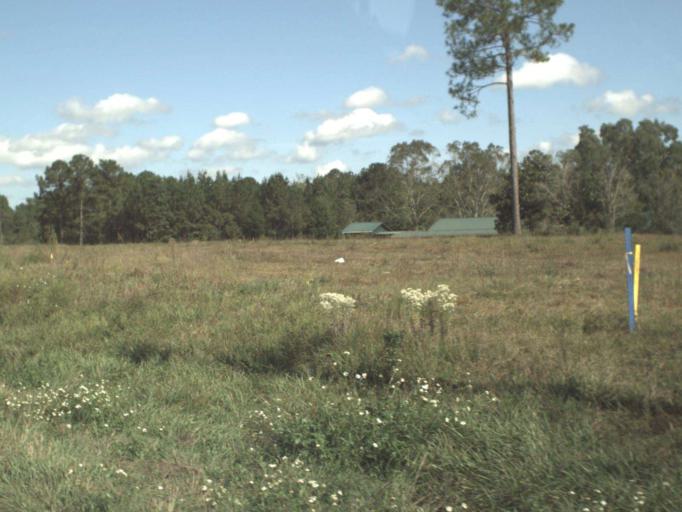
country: US
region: Florida
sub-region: Walton County
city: DeFuniak Springs
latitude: 30.6607
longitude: -86.1204
